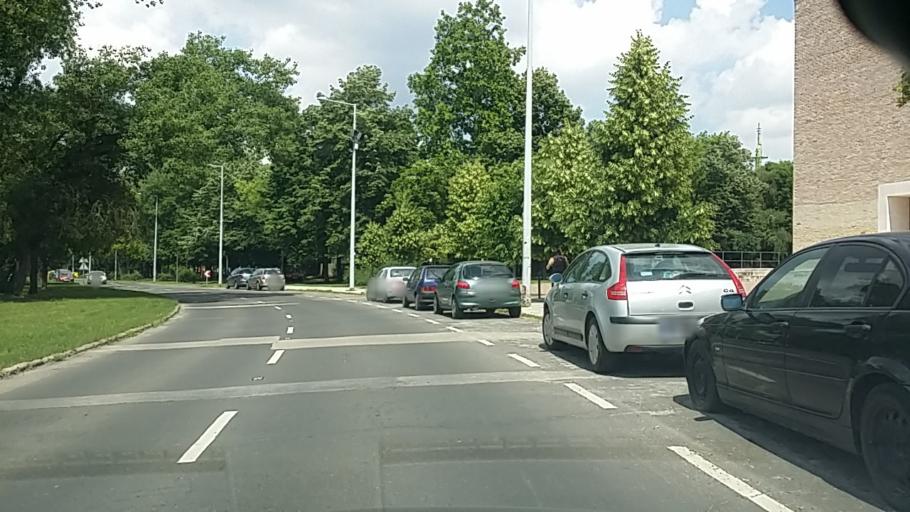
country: HU
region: Budapest
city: Budapest XV. keruelet
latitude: 47.5412
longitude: 19.1371
